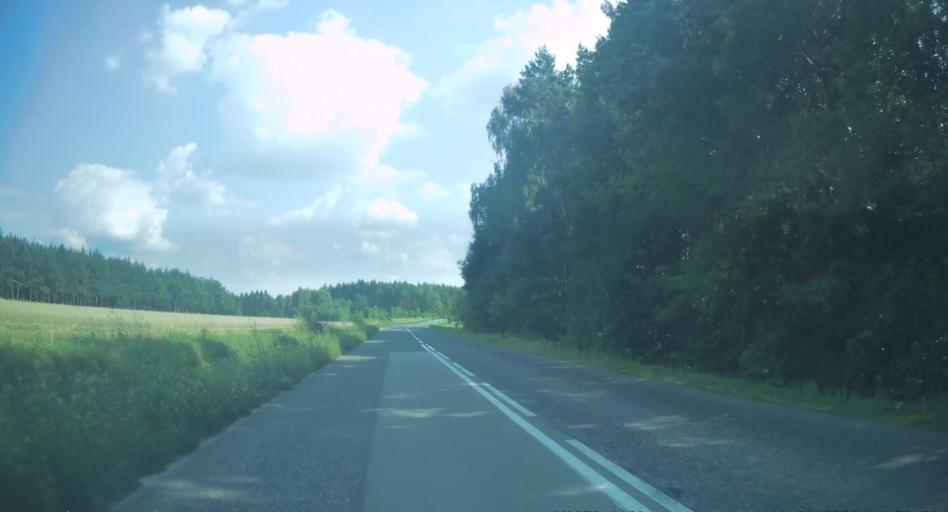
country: PL
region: Swietokrzyskie
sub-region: Powiat kielecki
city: Lopuszno
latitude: 50.8933
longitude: 20.2547
